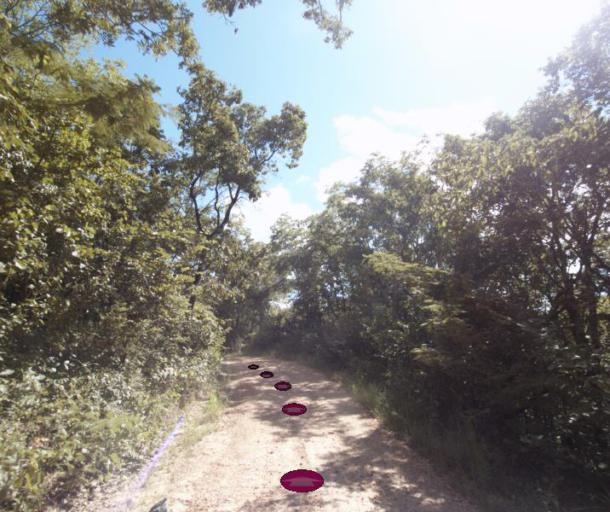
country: BR
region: Goias
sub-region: Pirenopolis
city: Pirenopolis
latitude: -15.7771
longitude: -48.9878
